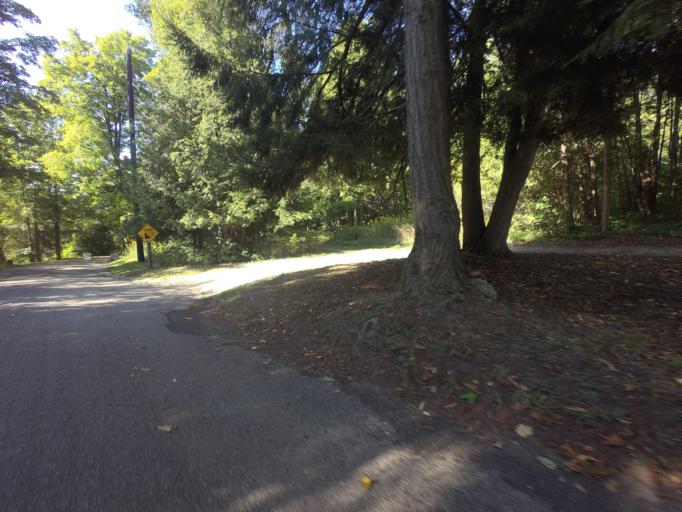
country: CA
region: Ontario
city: Waterloo
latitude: 43.6639
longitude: -80.4502
